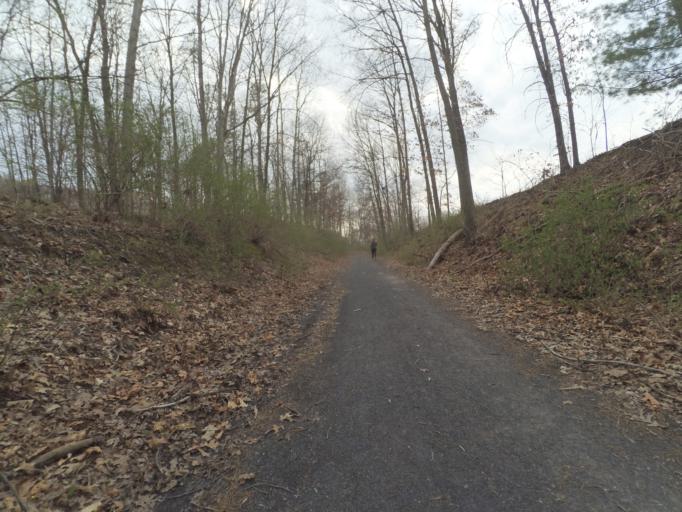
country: US
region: Pennsylvania
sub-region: Centre County
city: Park Forest Village
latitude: 40.8207
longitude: -77.8845
